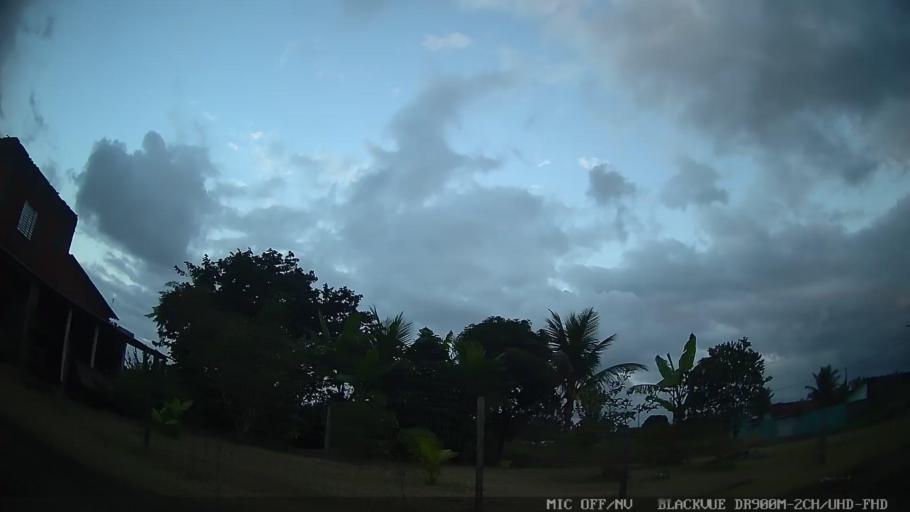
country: BR
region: Sao Paulo
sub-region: Itanhaem
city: Itanhaem
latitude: -24.1867
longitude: -46.8341
